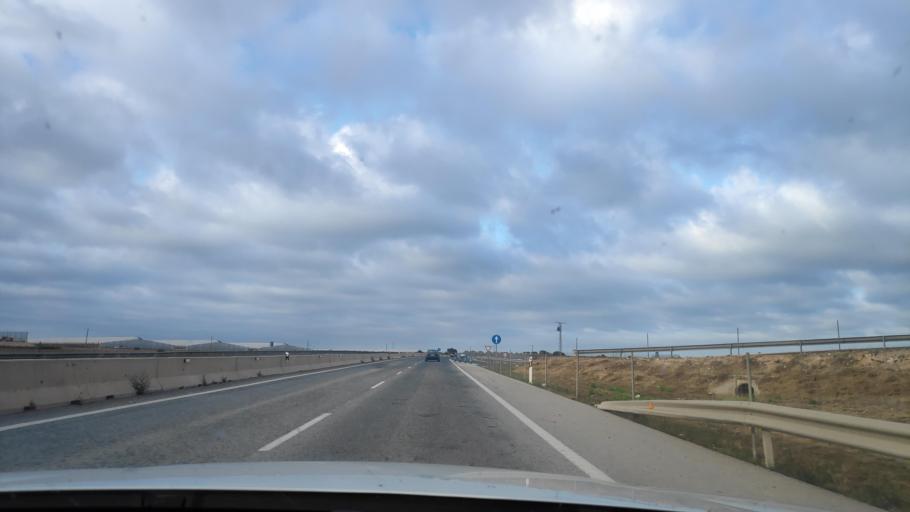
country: ES
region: Murcia
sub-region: Murcia
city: Torre-Pacheco
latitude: 37.8144
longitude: -0.9469
